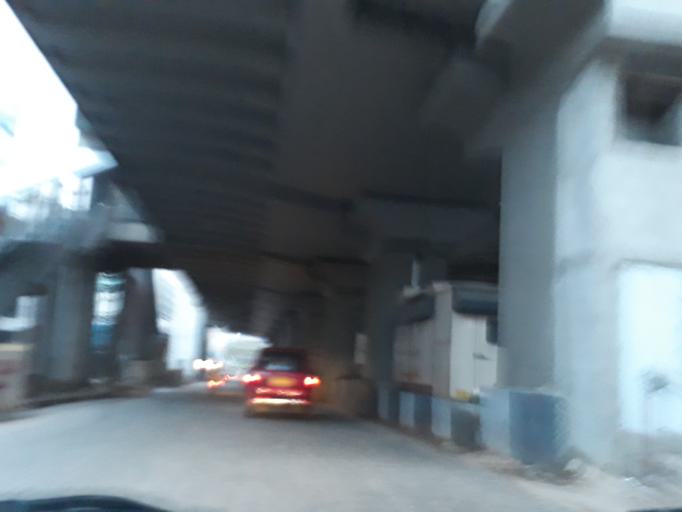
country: IN
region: Telangana
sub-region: Rangareddi
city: Kukatpalli
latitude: 17.4301
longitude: 78.4091
